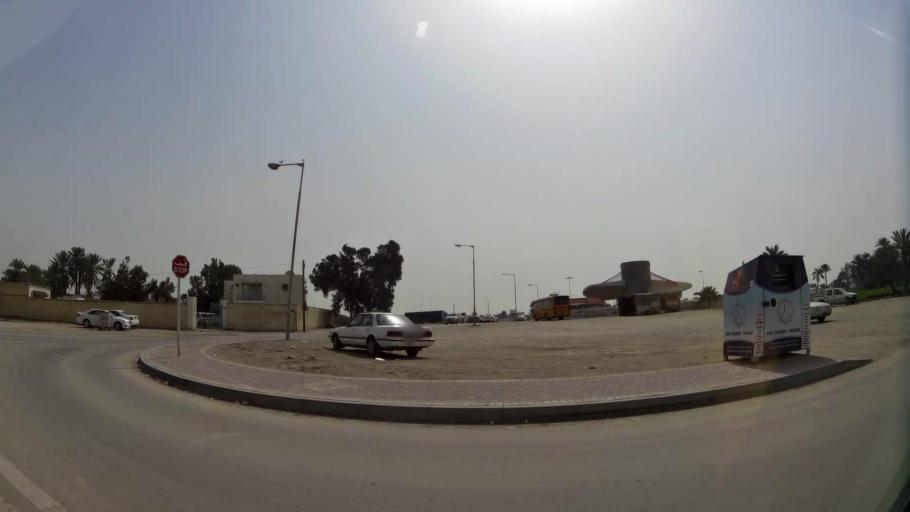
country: BH
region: Manama
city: Jidd Hafs
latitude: 26.2256
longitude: 50.5202
